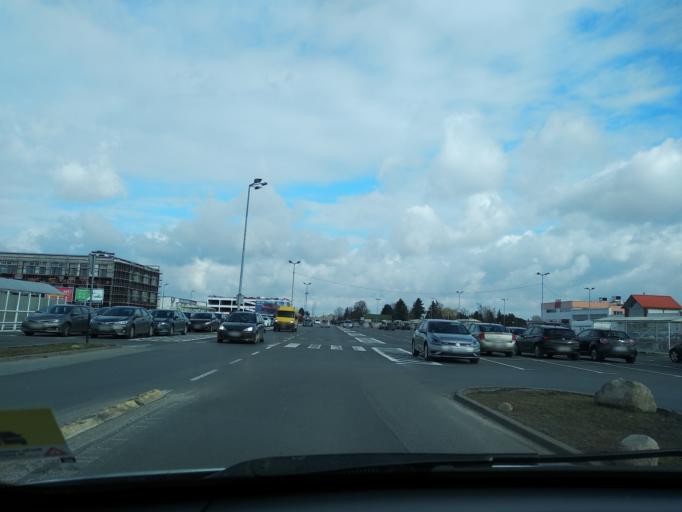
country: PL
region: Masovian Voivodeship
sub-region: Powiat piaseczynski
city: Mysiadlo
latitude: 52.0948
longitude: 21.0206
